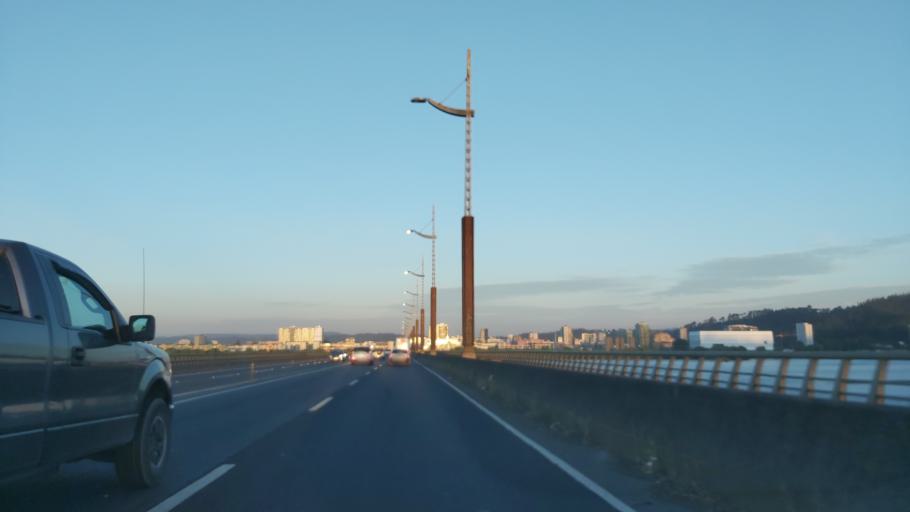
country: CL
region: Biobio
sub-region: Provincia de Concepcion
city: Concepcion
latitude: -36.8334
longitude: -73.0768
